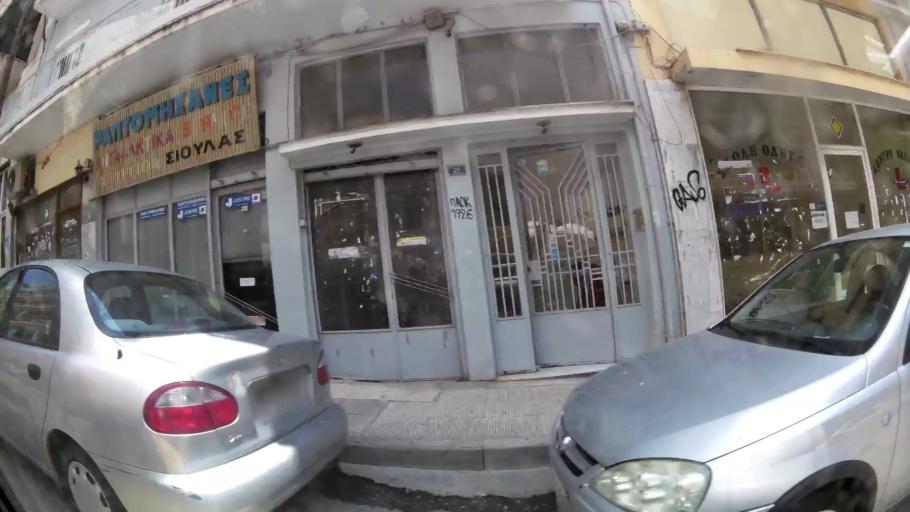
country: GR
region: West Macedonia
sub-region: Nomos Kozanis
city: Kozani
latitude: 40.2985
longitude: 21.7874
